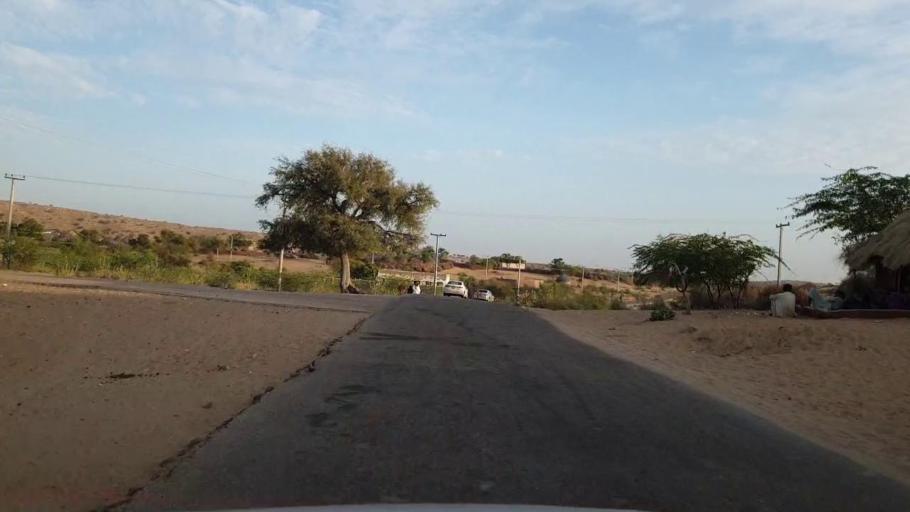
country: PK
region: Sindh
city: Nabisar
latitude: 25.0571
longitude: 69.9662
